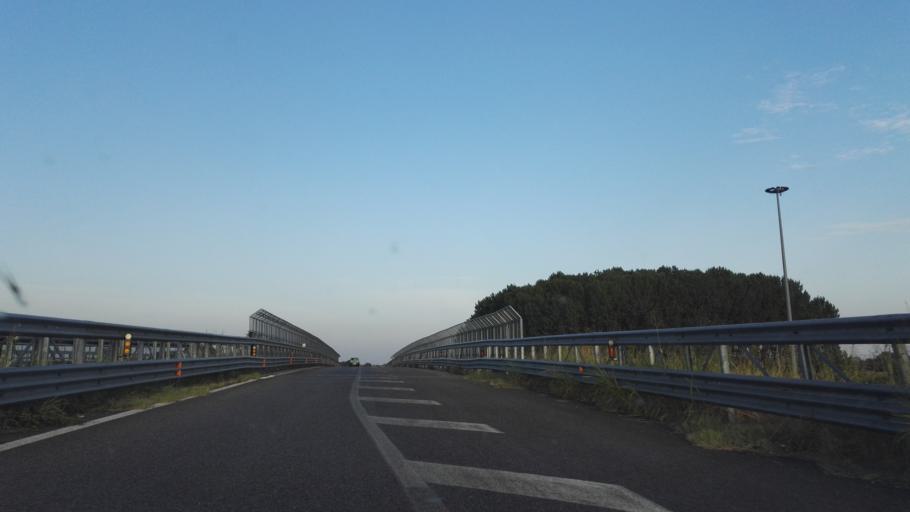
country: IT
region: Lombardy
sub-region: Citta metropolitana di Milano
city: Caleppio
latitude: 45.4291
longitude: 9.3738
